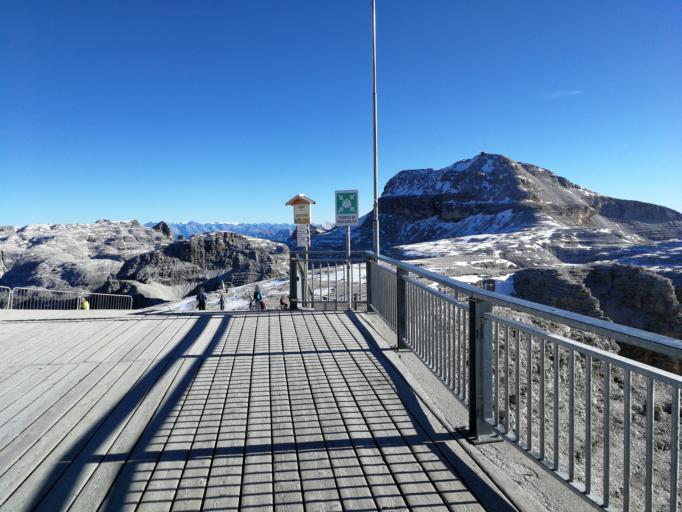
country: IT
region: Trentino-Alto Adige
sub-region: Provincia di Trento
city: Canazei
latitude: 46.5004
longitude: 11.8080
